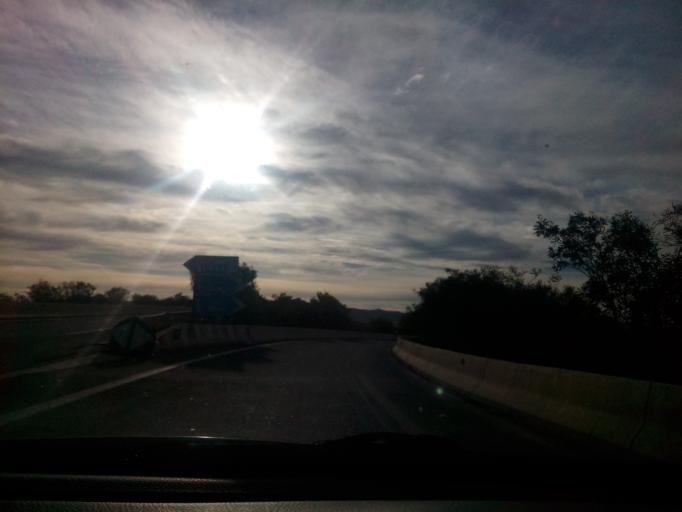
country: DZ
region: Mascara
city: Mascara
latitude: 35.6256
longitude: 0.0739
